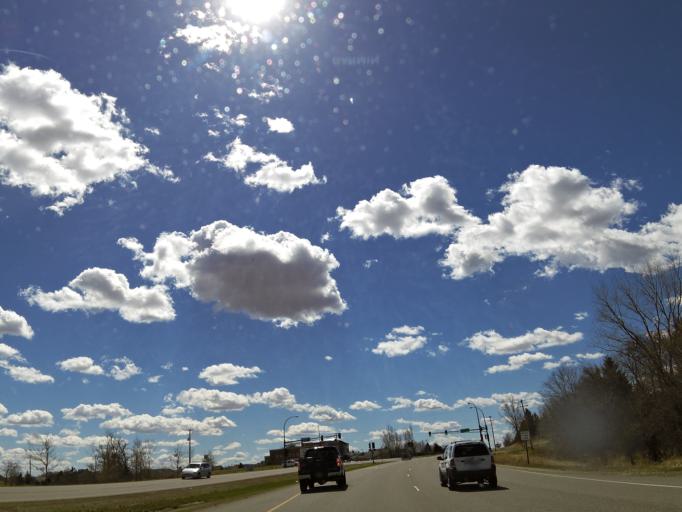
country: US
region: Minnesota
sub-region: Washington County
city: Woodbury
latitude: 44.9160
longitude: -92.9343
